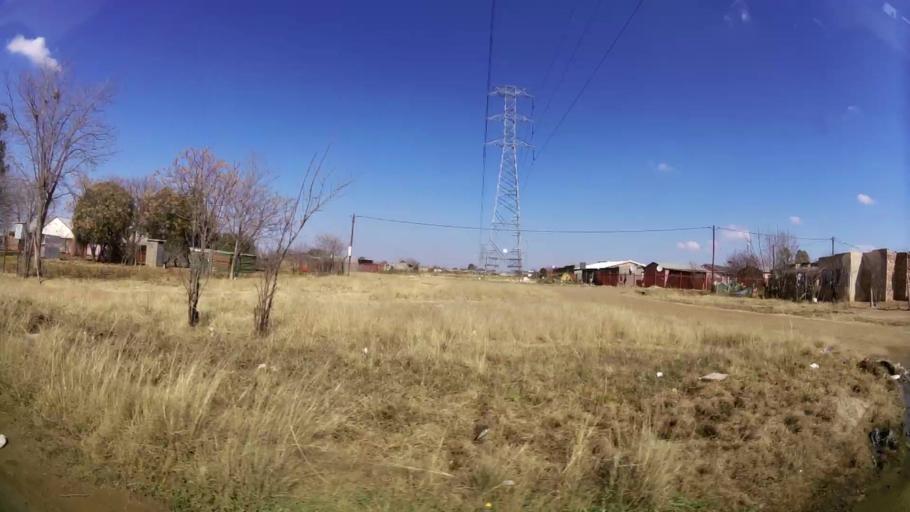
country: ZA
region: Orange Free State
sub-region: Mangaung Metropolitan Municipality
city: Bloemfontein
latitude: -29.1494
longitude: 26.2865
